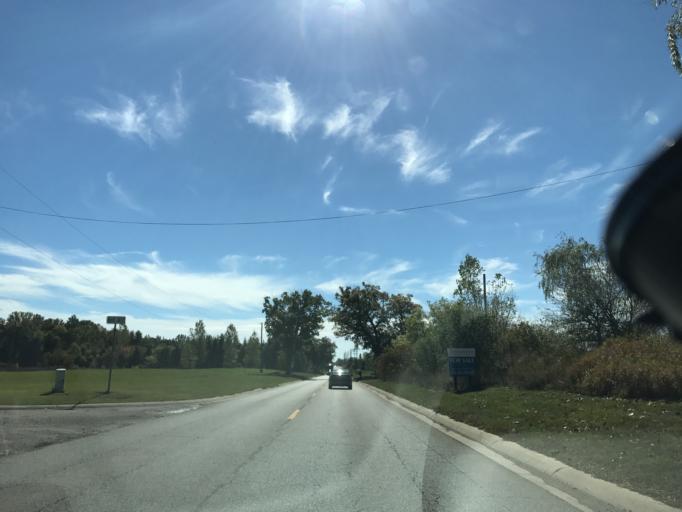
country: US
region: Michigan
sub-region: Oakland County
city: South Lyon
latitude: 42.4563
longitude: -83.6315
